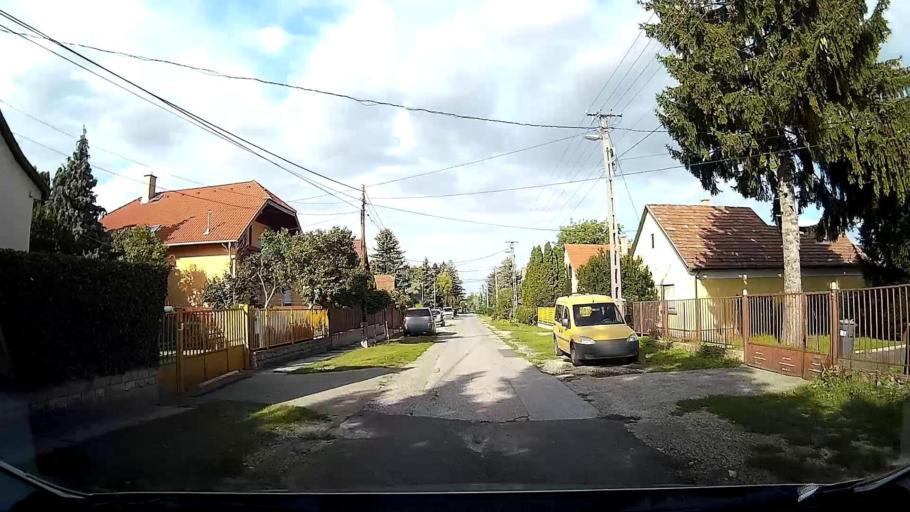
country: HU
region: Pest
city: Pomaz
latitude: 47.6380
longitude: 19.0305
